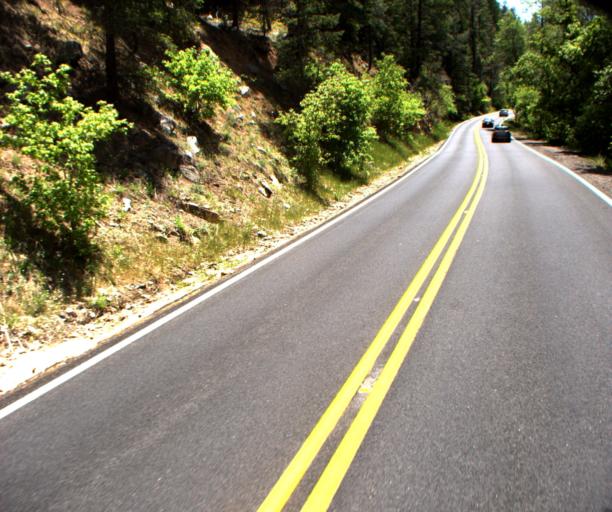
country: US
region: Arizona
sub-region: Coconino County
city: Kachina Village
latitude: 35.0232
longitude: -111.7362
